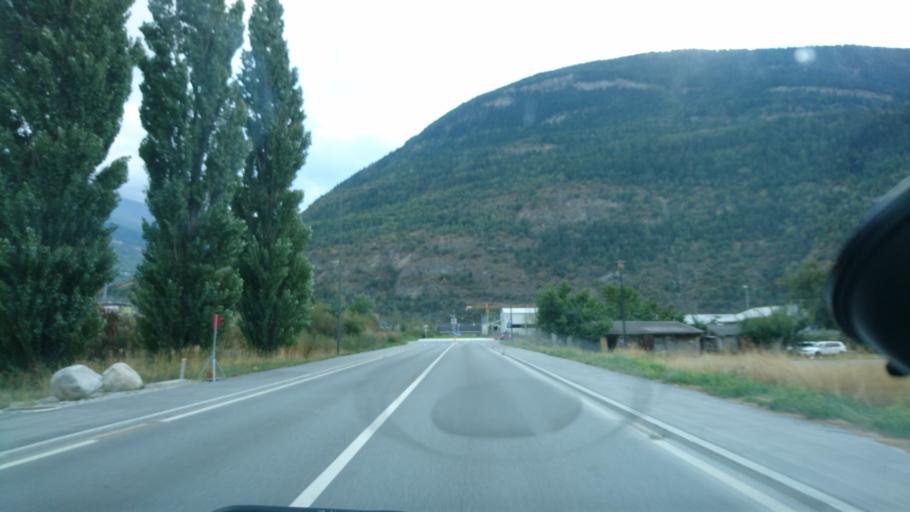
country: CH
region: Valais
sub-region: Visp District
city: Baltschieder
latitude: 46.3013
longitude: 7.8663
